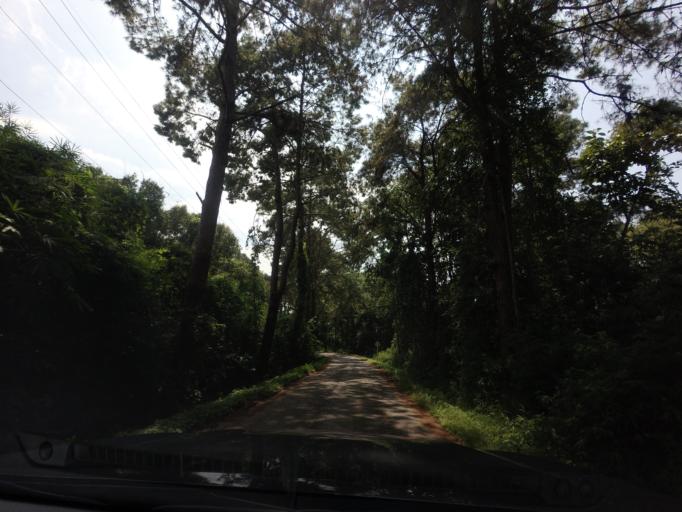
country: TH
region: Loei
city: Phu Ruea
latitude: 17.4773
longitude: 101.3522
